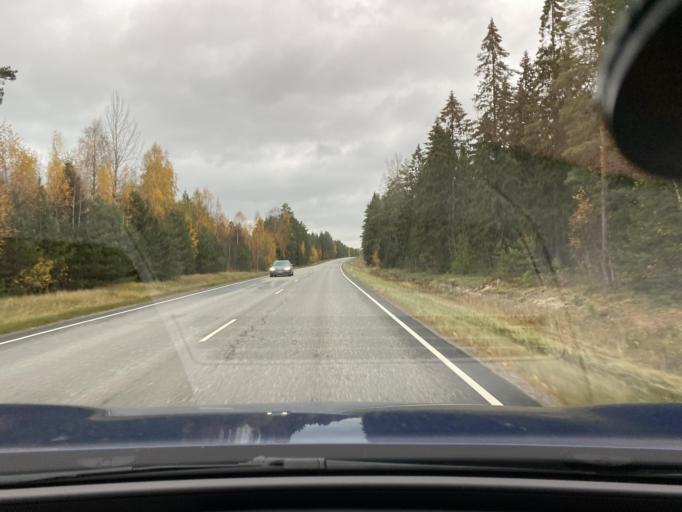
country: FI
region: Varsinais-Suomi
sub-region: Loimaa
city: Ylaene
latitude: 60.9045
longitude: 22.4083
